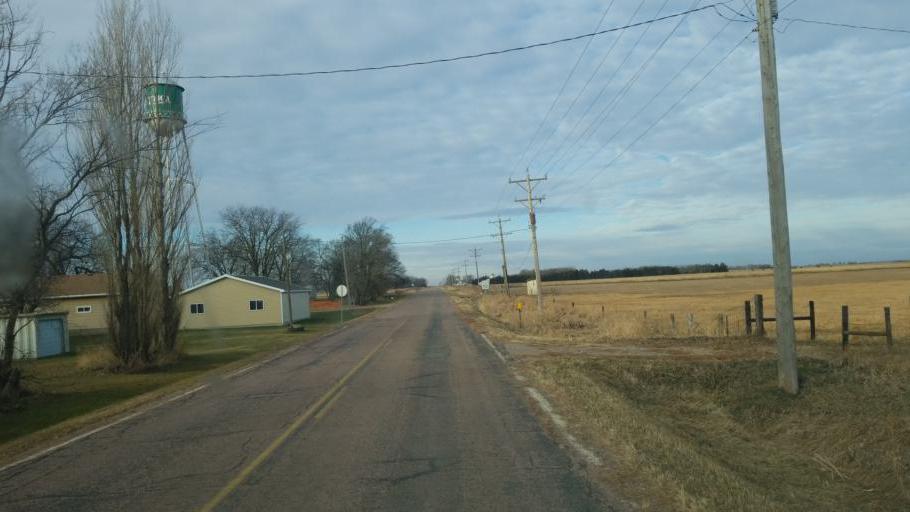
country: US
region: South Dakota
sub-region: Yankton County
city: Yankton
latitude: 42.9812
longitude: -97.4989
